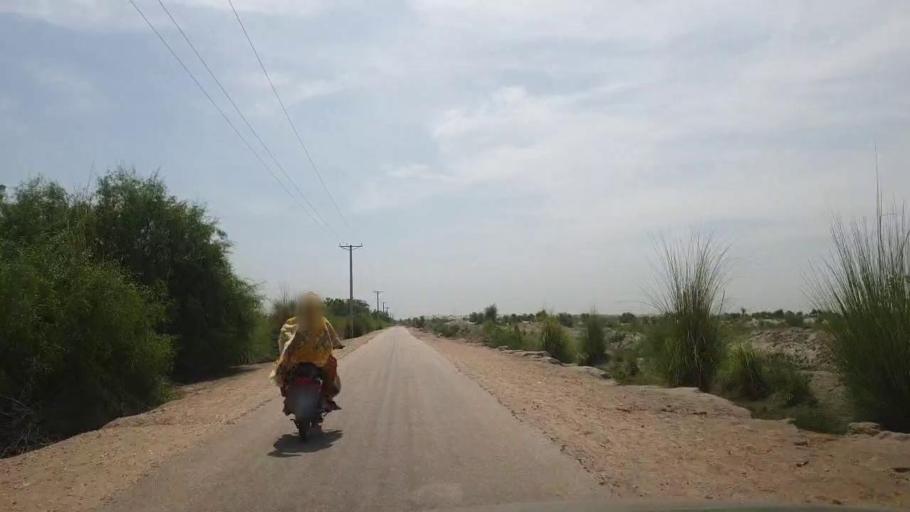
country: PK
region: Sindh
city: Kot Diji
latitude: 27.1160
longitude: 69.0110
